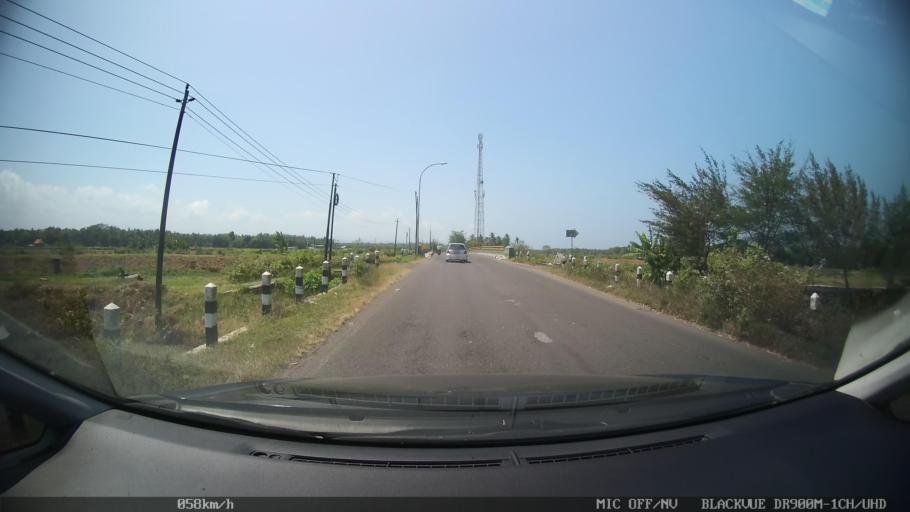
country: ID
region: Daerah Istimewa Yogyakarta
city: Srandakan
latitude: -7.9514
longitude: 110.1903
